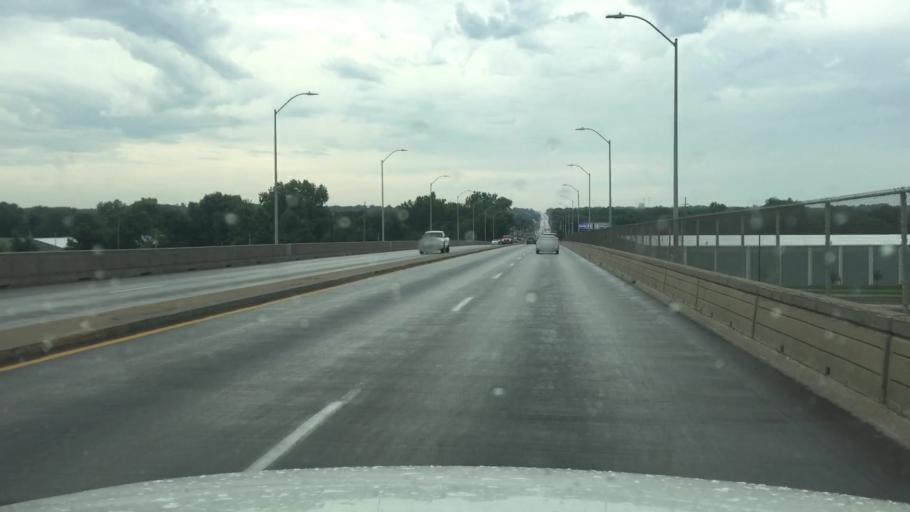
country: US
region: Iowa
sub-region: Polk County
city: Des Moines
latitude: 41.5861
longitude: -93.5969
